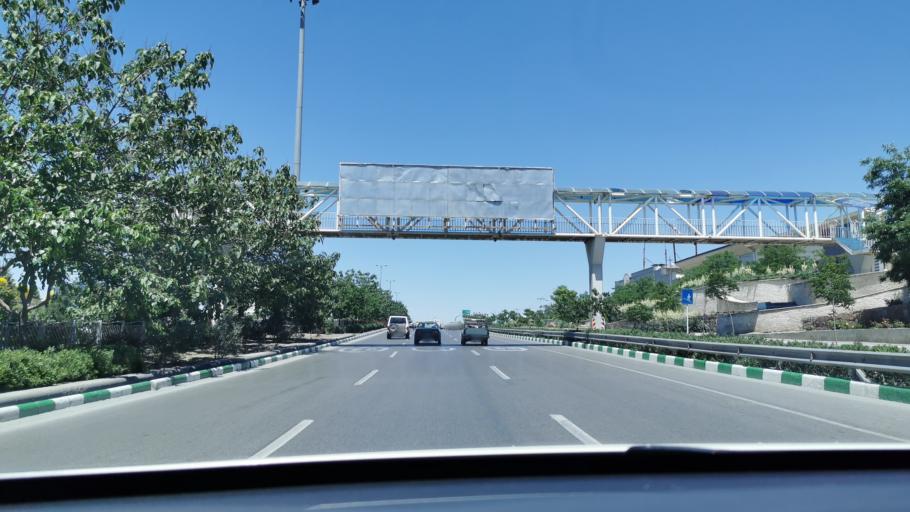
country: IR
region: Razavi Khorasan
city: Mashhad
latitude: 36.2634
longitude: 59.6518
